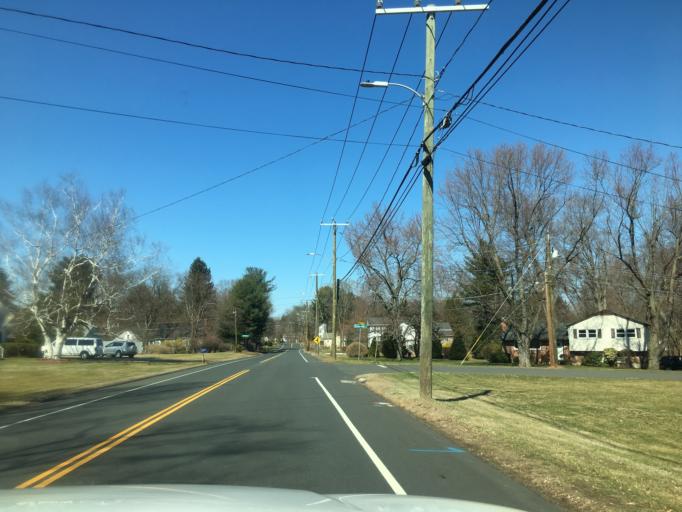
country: US
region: Connecticut
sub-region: Hartford County
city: Windsor
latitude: 41.8851
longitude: -72.6688
